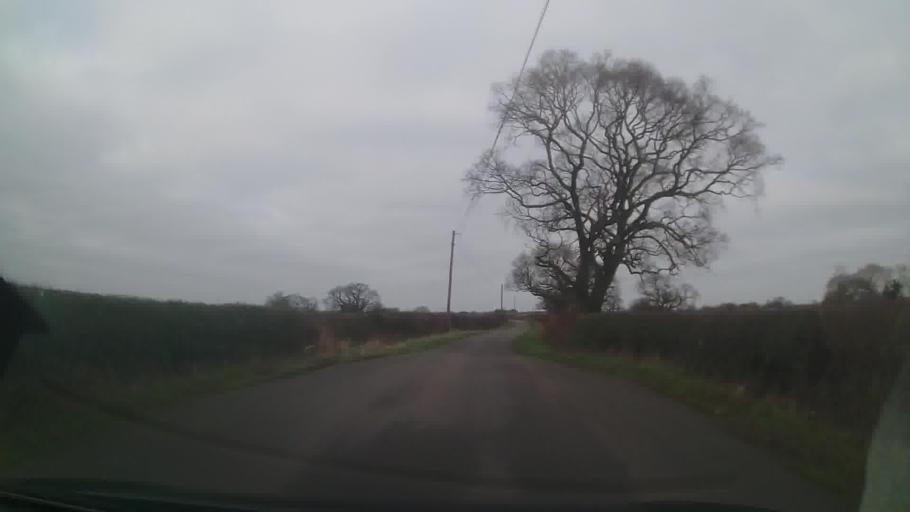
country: GB
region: England
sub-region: Shropshire
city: Petton
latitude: 52.8246
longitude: -2.7902
